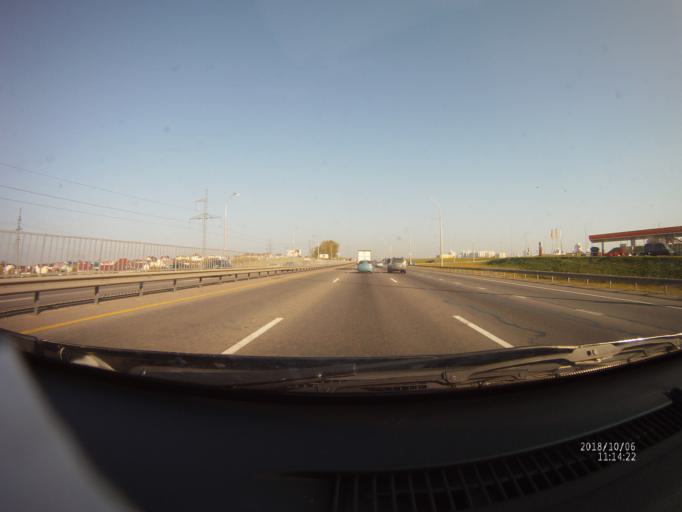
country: BY
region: Minsk
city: Zhdanovichy
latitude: 53.9171
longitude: 27.4125
